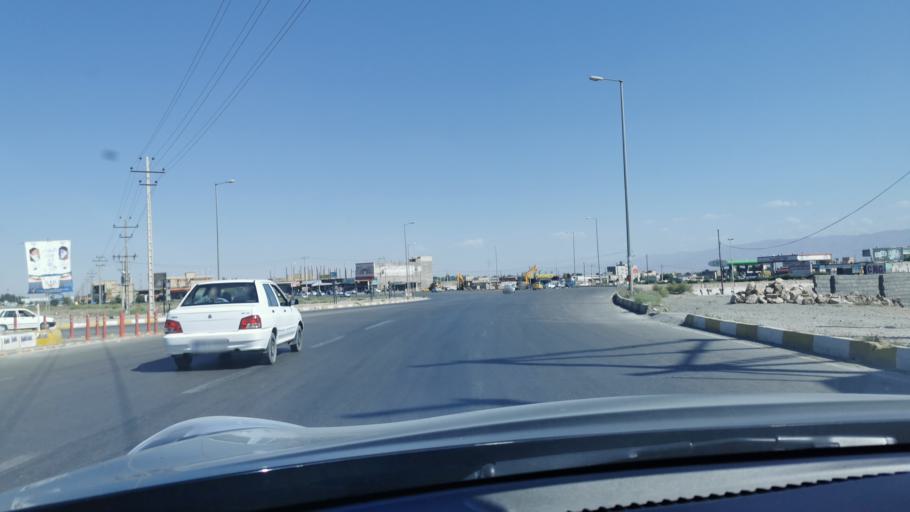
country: IR
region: Razavi Khorasan
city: Chenaran
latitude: 36.6330
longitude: 59.1329
